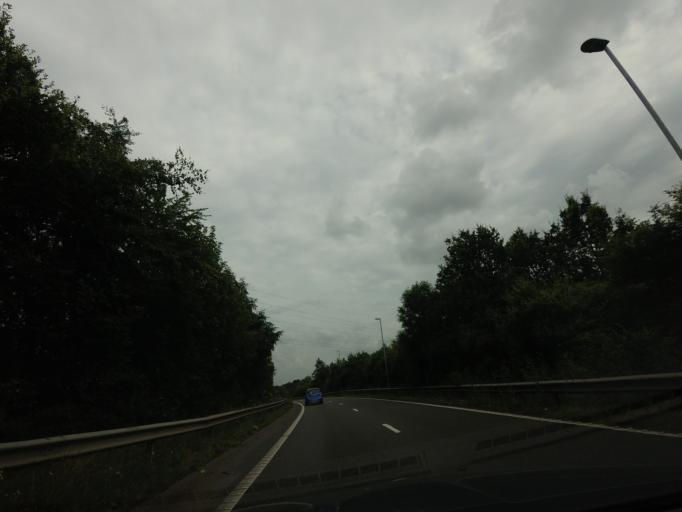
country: GB
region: England
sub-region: Shropshire
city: Shifnal
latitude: 52.6798
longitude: -2.4053
